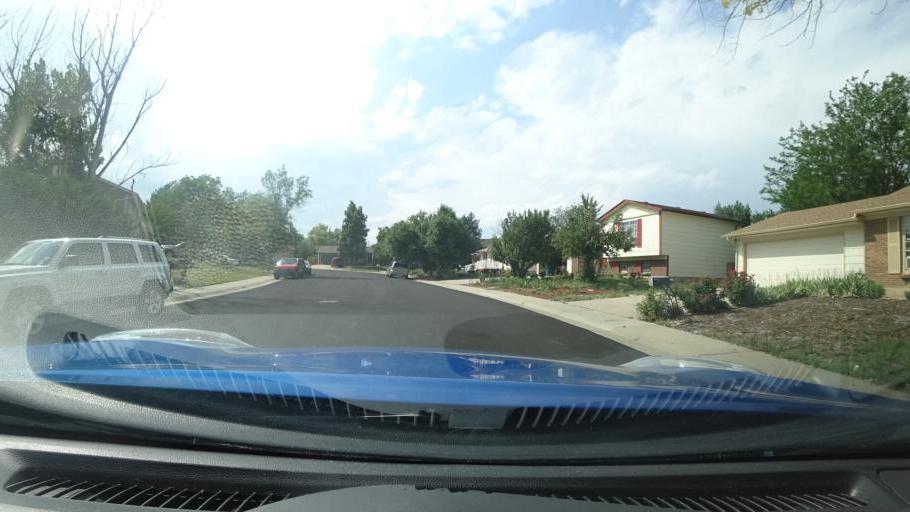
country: US
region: Colorado
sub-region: Adams County
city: Aurora
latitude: 39.6883
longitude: -104.7818
